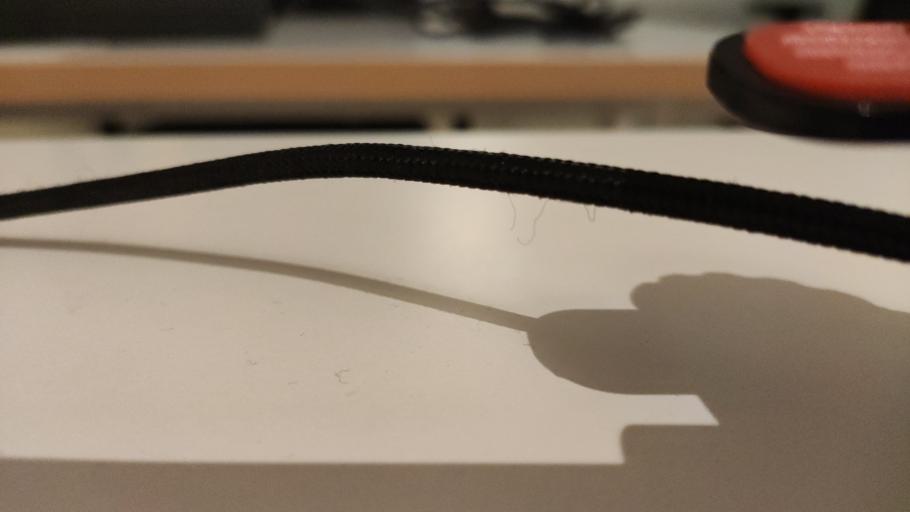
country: RU
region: Moskovskaya
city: Il'inskiy Pogost
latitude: 55.5191
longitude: 38.8717
